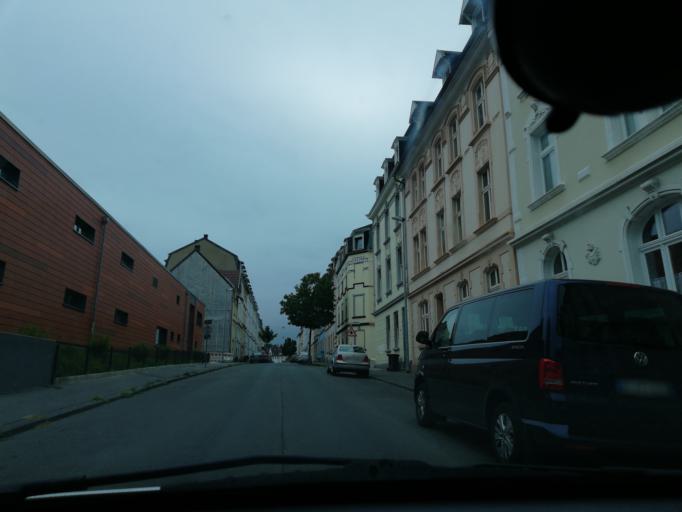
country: DE
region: North Rhine-Westphalia
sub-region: Regierungsbezirk Dusseldorf
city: Wuppertal
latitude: 51.2687
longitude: 7.2247
